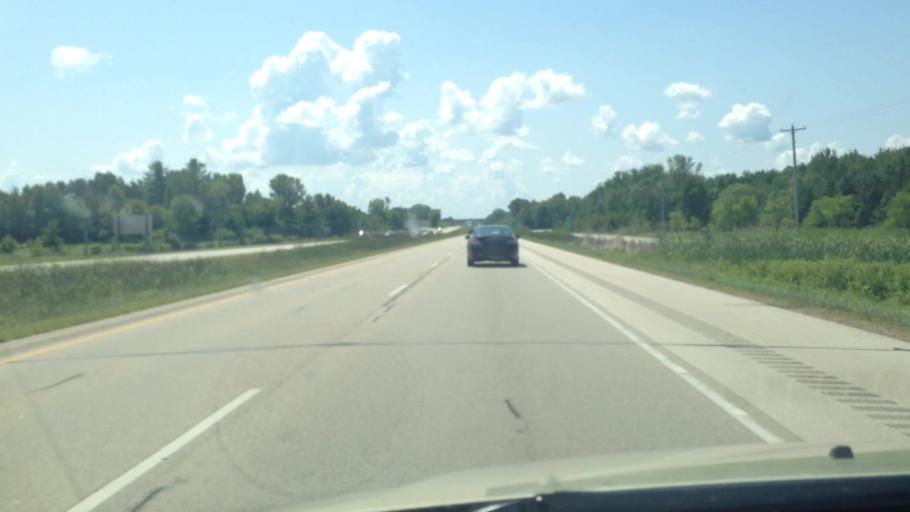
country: US
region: Wisconsin
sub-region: Brown County
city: Suamico
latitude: 44.7306
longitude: -88.0510
